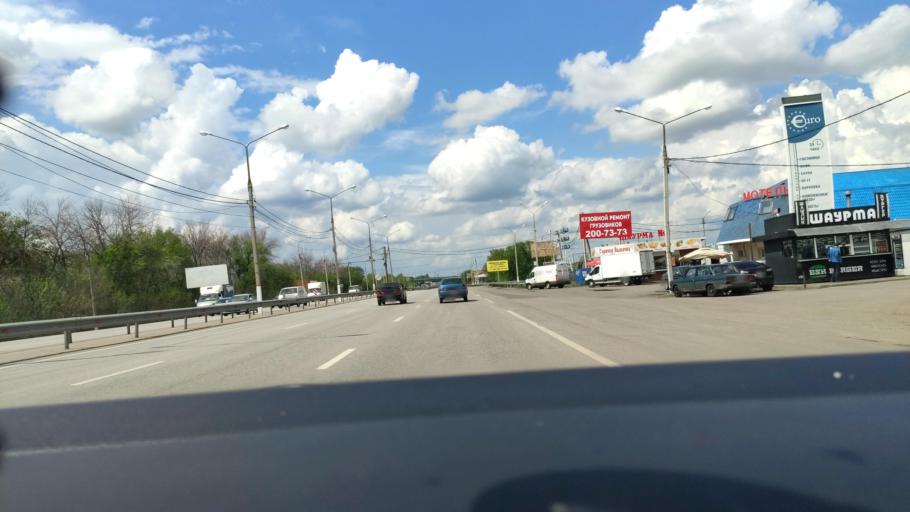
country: RU
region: Voronezj
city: Novaya Usman'
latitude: 51.6393
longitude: 39.3248
